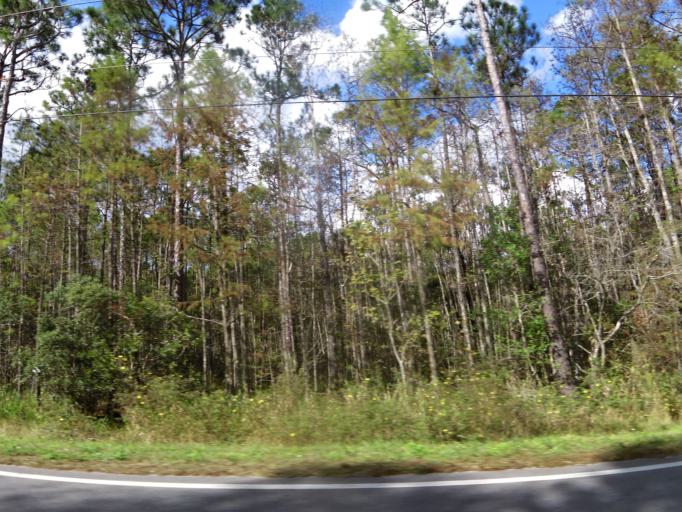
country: US
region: Florida
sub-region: Saint Johns County
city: Villano Beach
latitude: 30.0103
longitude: -81.3994
